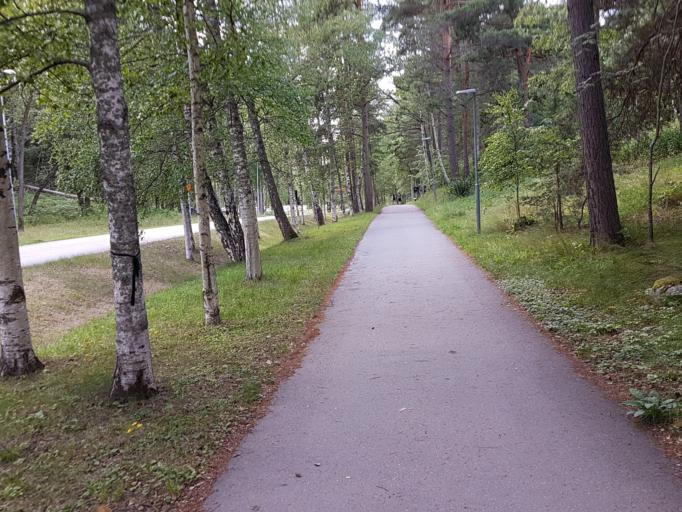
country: SE
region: Stockholm
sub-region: Nacka Kommun
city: Kummelnas
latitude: 59.3446
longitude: 18.2451
